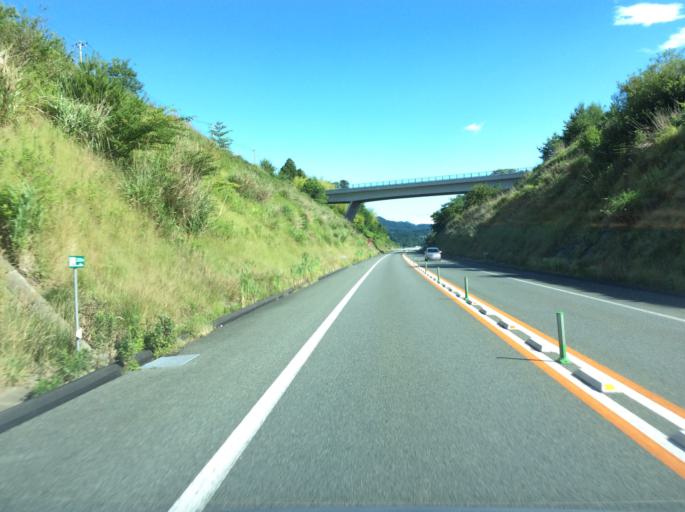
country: JP
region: Fukushima
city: Namie
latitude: 37.2685
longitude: 140.9858
